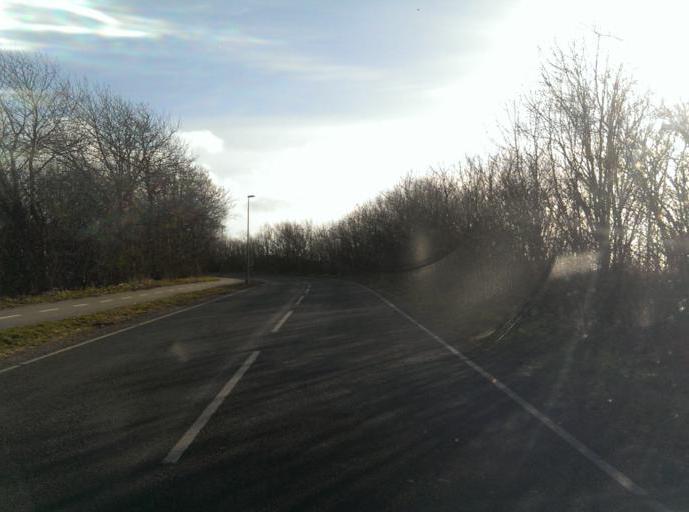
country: DK
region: South Denmark
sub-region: Esbjerg Kommune
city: Bramming
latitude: 55.4261
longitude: 8.6525
